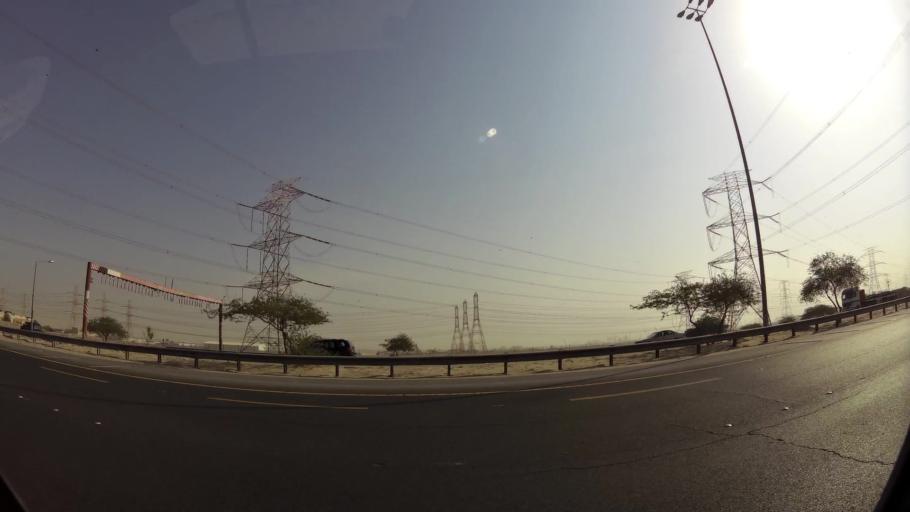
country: KW
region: Al Ahmadi
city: Al Ahmadi
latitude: 29.0025
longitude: 48.0961
